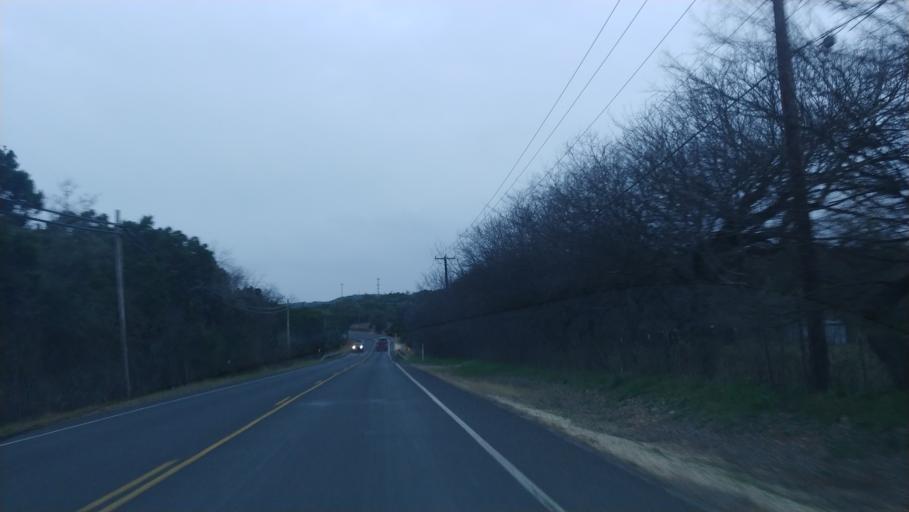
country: US
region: Texas
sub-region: Bexar County
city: Helotes
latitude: 29.5977
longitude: -98.6881
